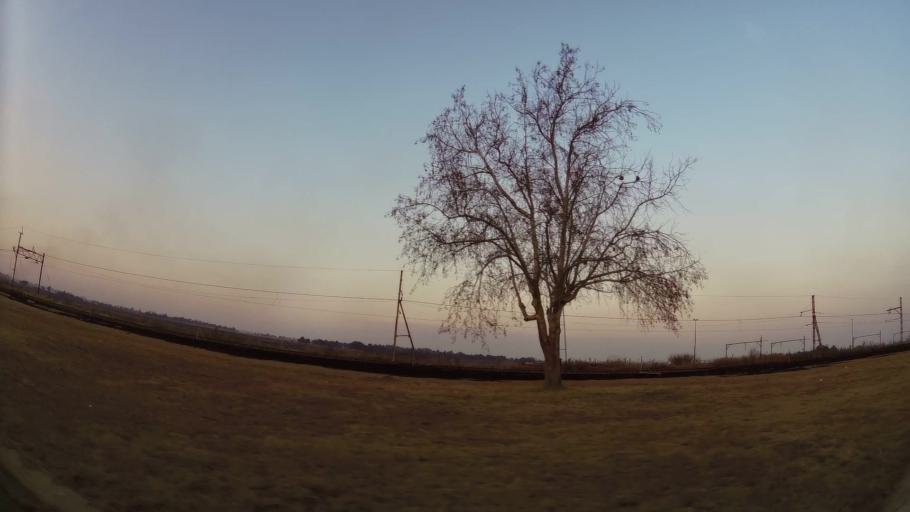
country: ZA
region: Gauteng
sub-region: Ekurhuleni Metropolitan Municipality
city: Nigel
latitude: -26.3467
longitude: 28.4409
